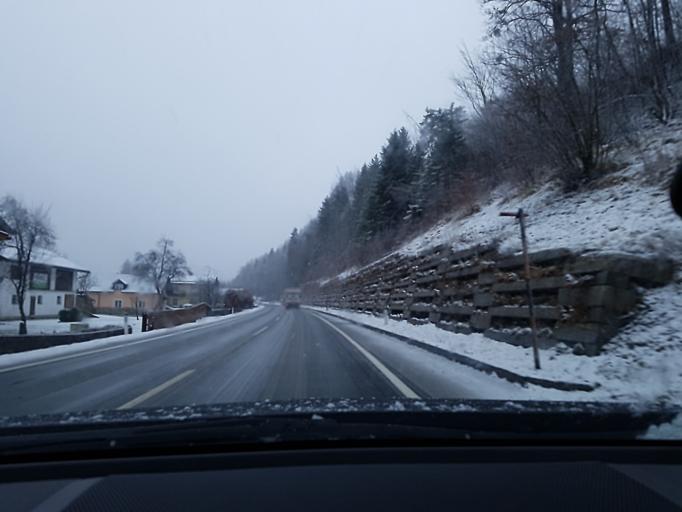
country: AT
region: Salzburg
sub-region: Politischer Bezirk Hallein
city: Scheffau am Tennengebirge
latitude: 47.5793
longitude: 13.2638
